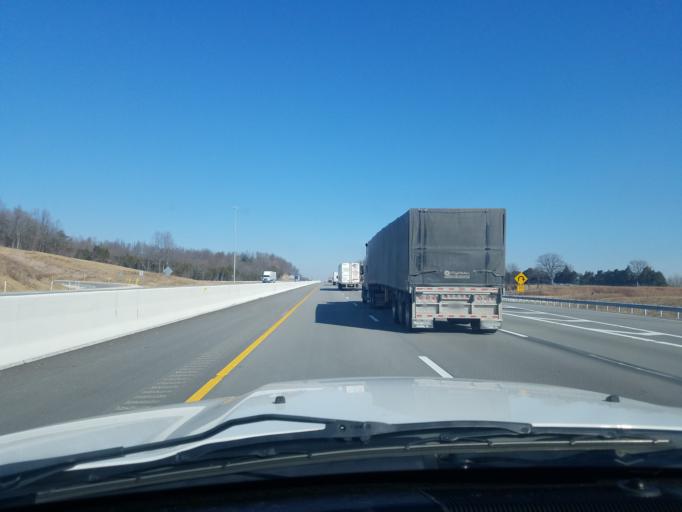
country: US
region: Kentucky
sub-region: Hart County
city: Munfordville
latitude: 37.3800
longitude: -85.8882
